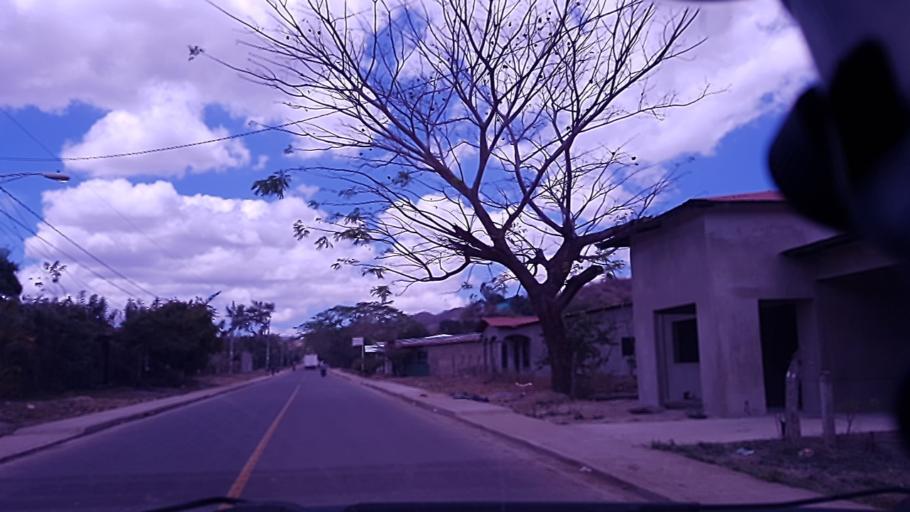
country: NI
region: Esteli
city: Condega
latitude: 13.3756
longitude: -86.3923
